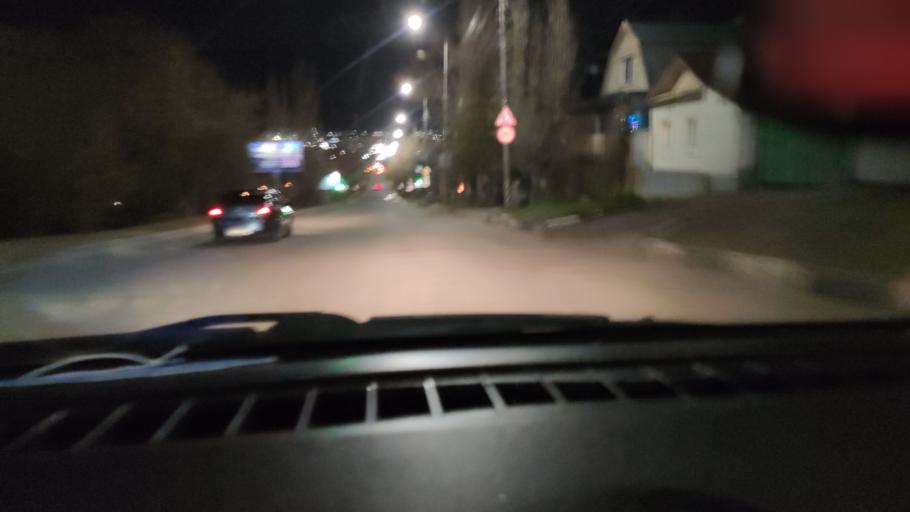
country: RU
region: Saratov
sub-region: Saratovskiy Rayon
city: Saratov
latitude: 51.5406
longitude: 46.0478
